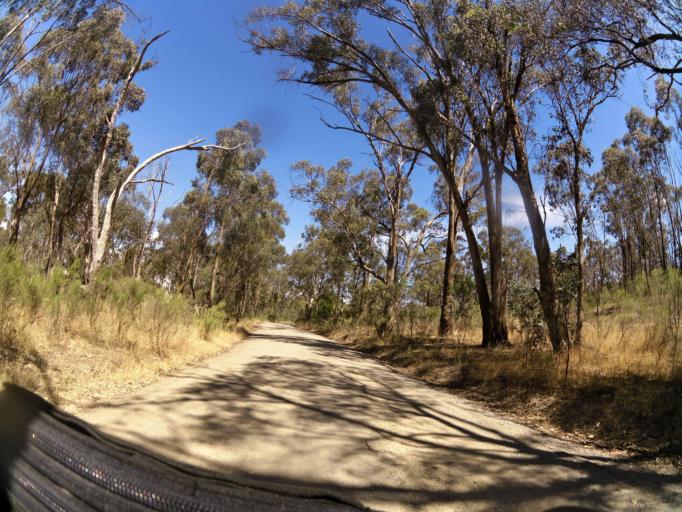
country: AU
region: Victoria
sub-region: Campaspe
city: Kyabram
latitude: -36.8535
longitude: 145.0658
